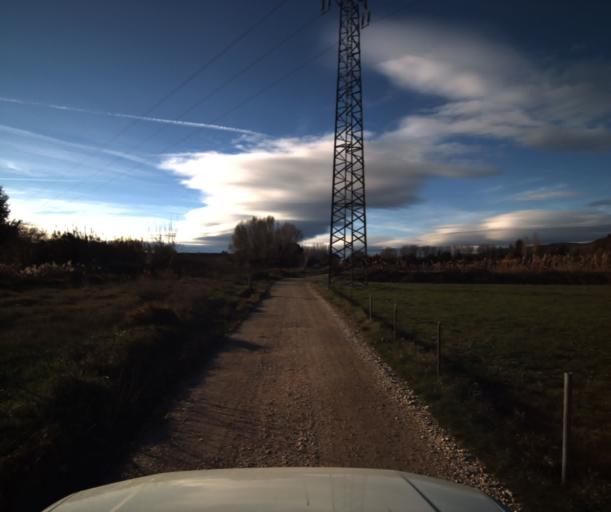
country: FR
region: Provence-Alpes-Cote d'Azur
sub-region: Departement du Vaucluse
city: Pertuis
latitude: 43.6917
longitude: 5.4841
